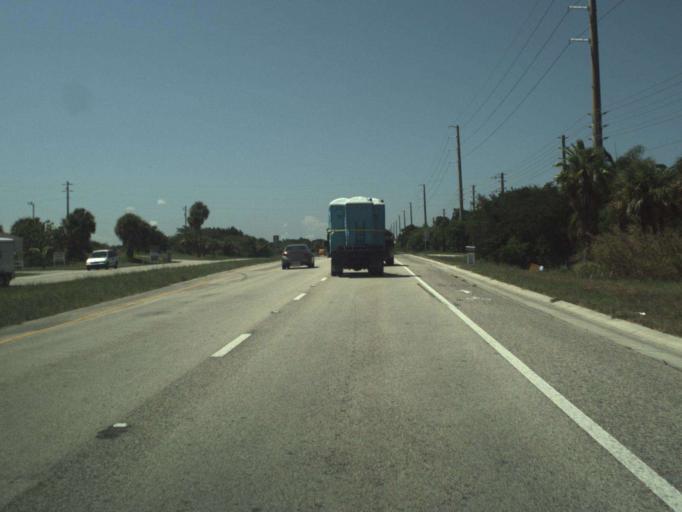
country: US
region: Florida
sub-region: Saint Lucie County
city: Fort Pierce North
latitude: 27.5071
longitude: -80.3487
